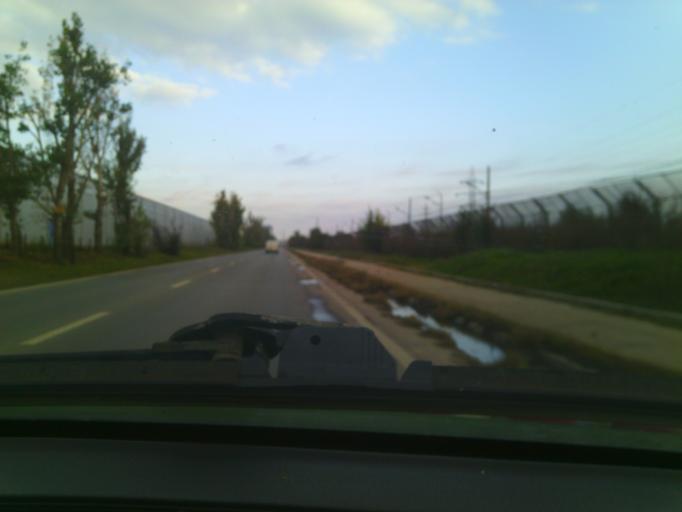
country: RO
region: Ilfov
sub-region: Comuna Popesti-Leordeni
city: Popesti-Leordeni
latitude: 44.3532
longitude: 26.1551
